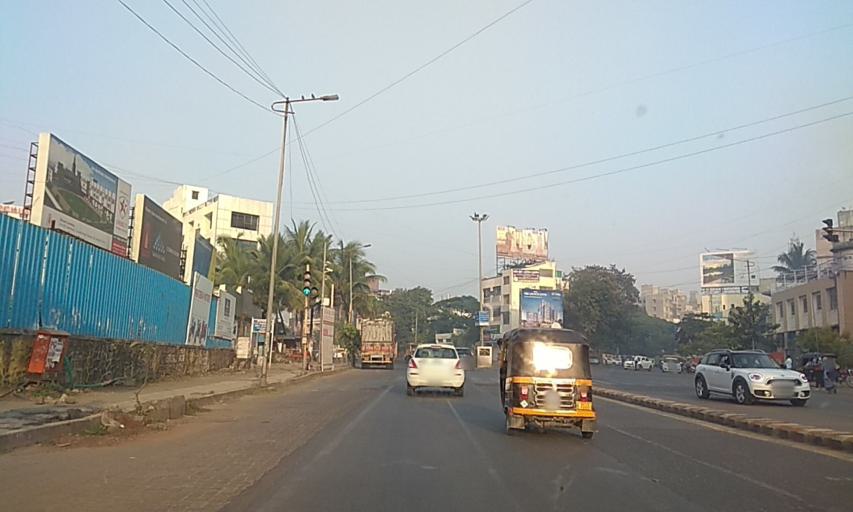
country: IN
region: Maharashtra
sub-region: Pune Division
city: Pimpri
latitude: 18.5632
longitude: 73.7831
